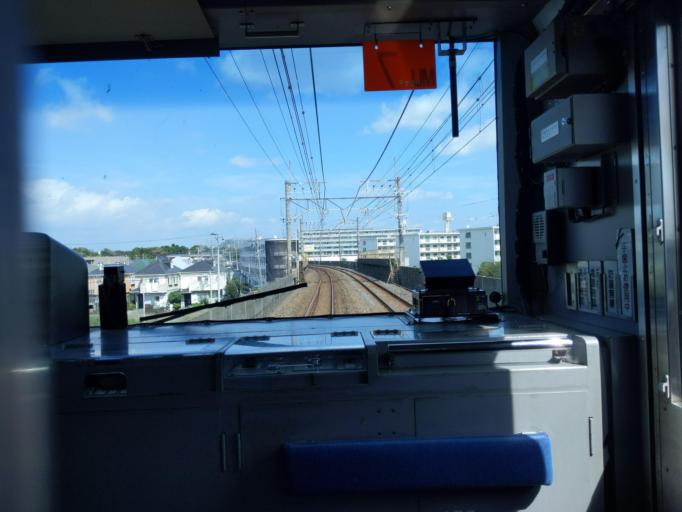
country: JP
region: Chiba
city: Funabashi
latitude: 35.7194
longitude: 139.9667
